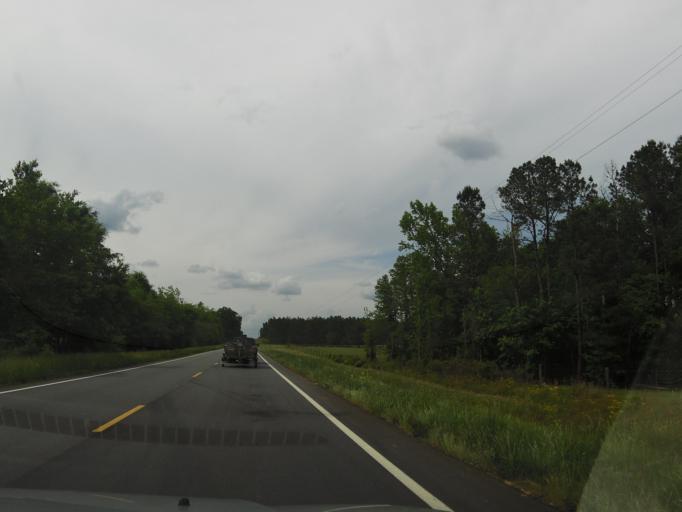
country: US
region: Georgia
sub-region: McDuffie County
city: Thomson
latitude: 33.3838
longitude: -82.4721
